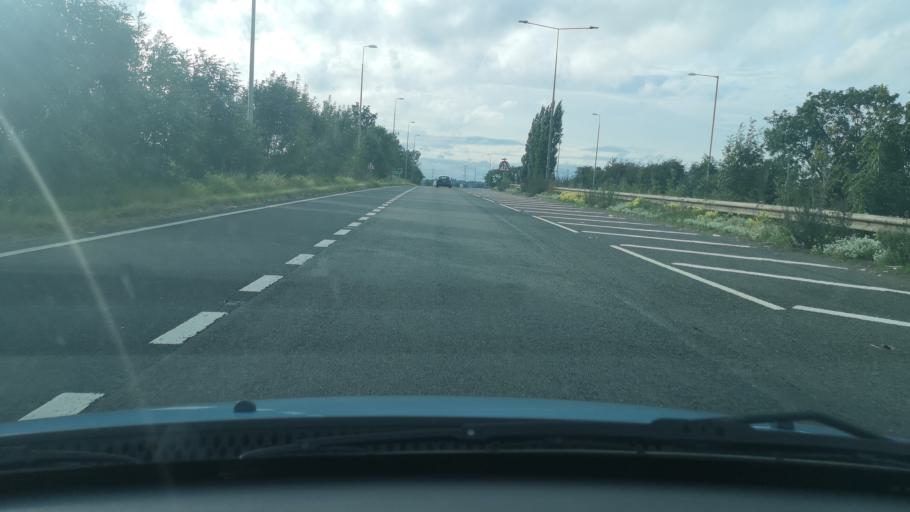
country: GB
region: England
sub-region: Doncaster
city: Marr
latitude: 53.5805
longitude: -1.2217
